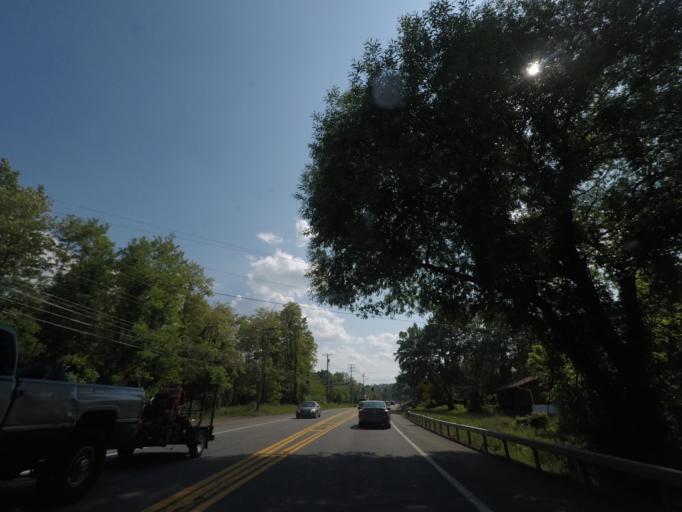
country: US
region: New York
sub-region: Orange County
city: Balmville
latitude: 41.5682
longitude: -73.9948
